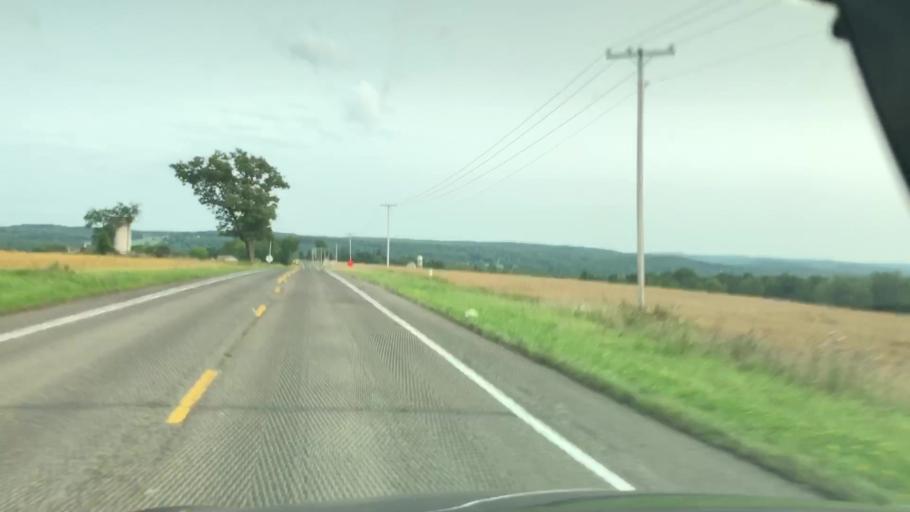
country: US
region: Pennsylvania
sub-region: Crawford County
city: Titusville
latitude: 41.7499
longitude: -79.7702
